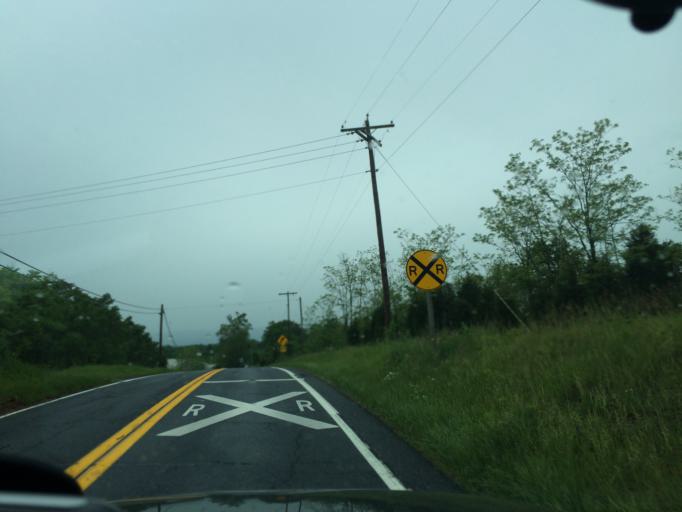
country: US
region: Maryland
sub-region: Frederick County
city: Woodsboro
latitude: 39.6054
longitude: -77.3261
